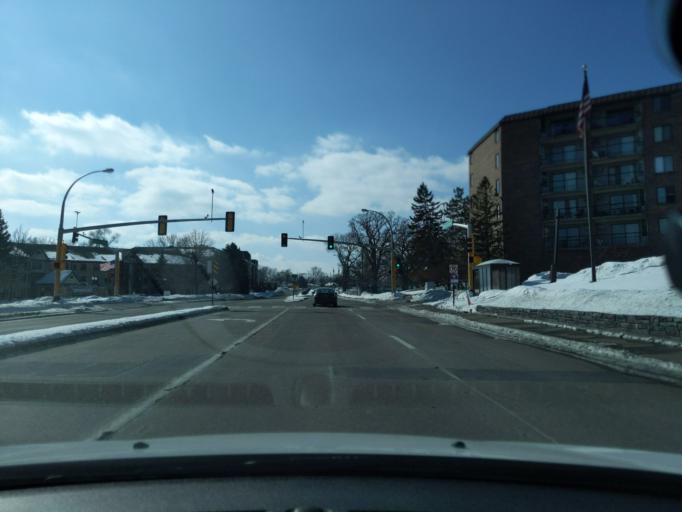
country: US
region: Minnesota
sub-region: Hennepin County
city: Saint Anthony
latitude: 45.0156
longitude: -93.2217
